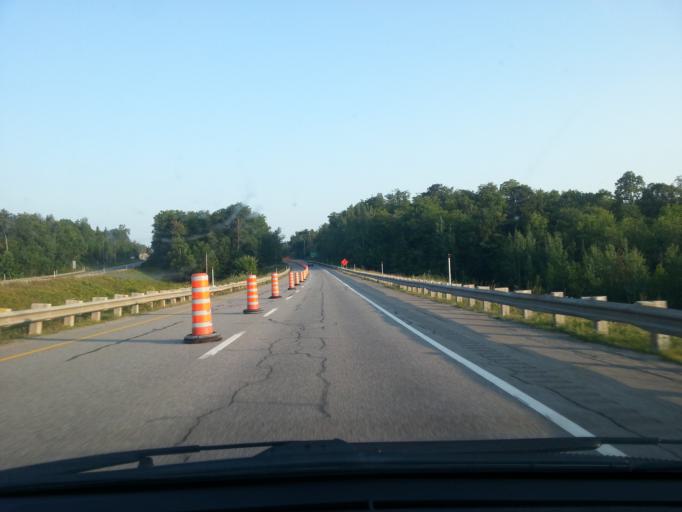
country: CA
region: Quebec
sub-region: Outaouais
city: Wakefield
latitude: 45.5682
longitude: -75.8647
